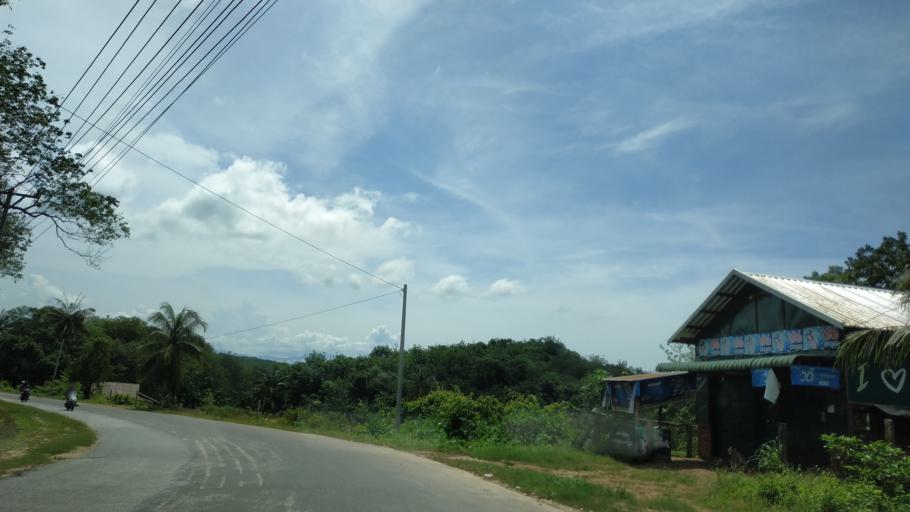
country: MM
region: Tanintharyi
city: Dawei
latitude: 14.1285
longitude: 98.1215
